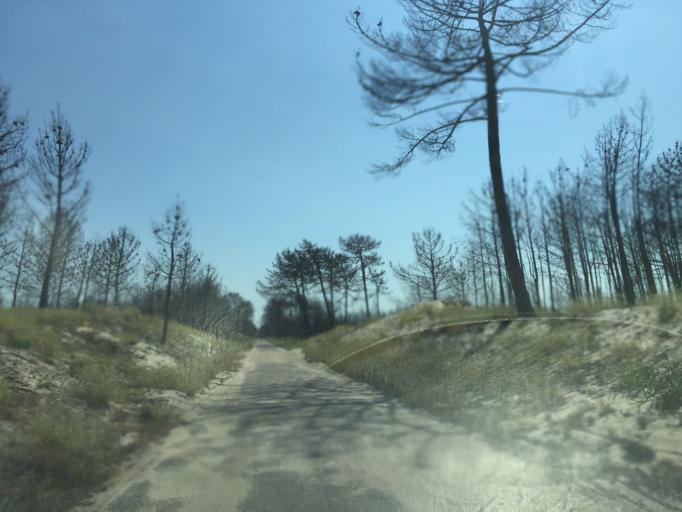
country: PT
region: Coimbra
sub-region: Figueira da Foz
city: Alhadas
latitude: 40.2711
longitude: -8.8303
